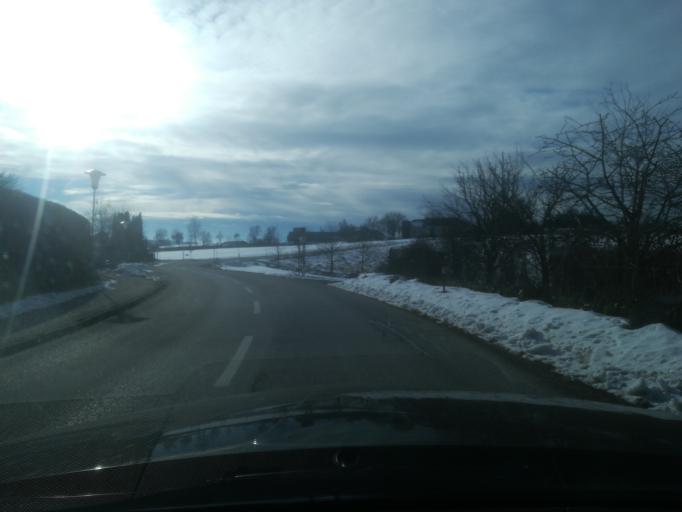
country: AT
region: Upper Austria
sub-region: Politischer Bezirk Perg
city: Perg
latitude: 48.3196
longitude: 14.6244
